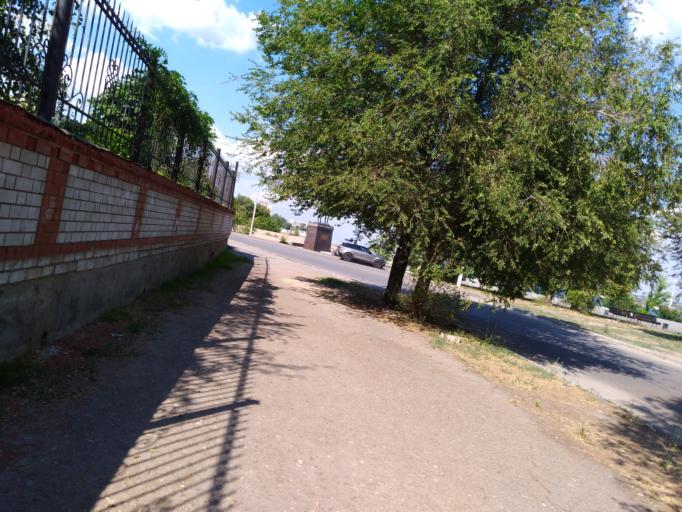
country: RU
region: Volgograd
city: Volgograd
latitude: 48.7199
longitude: 44.5382
